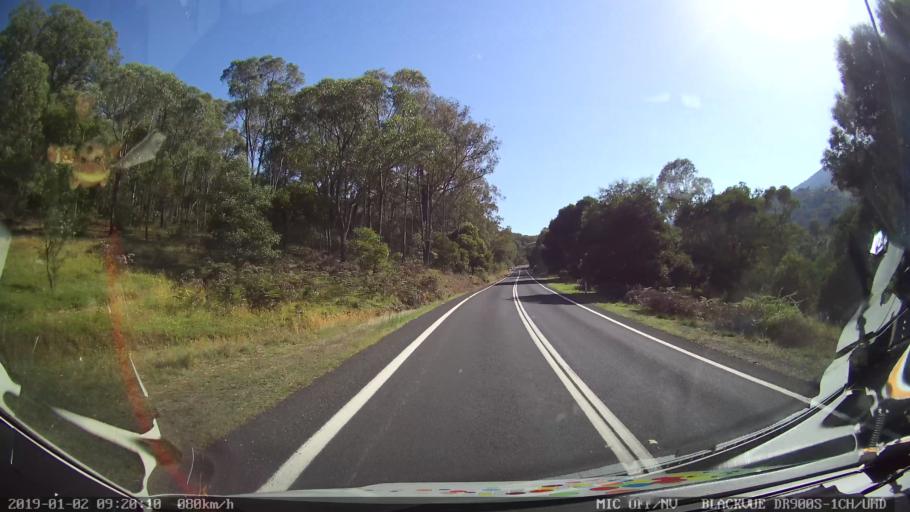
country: AU
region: New South Wales
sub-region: Tumut Shire
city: Tumut
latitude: -35.4147
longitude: 148.2810
